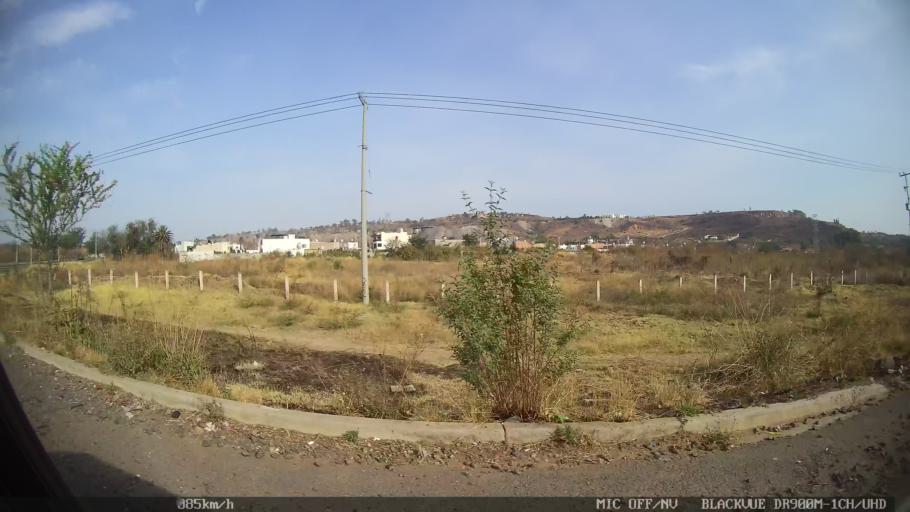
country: MX
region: Jalisco
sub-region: Tonala
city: Paseo de las Canadas
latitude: 20.6249
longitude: -103.2112
